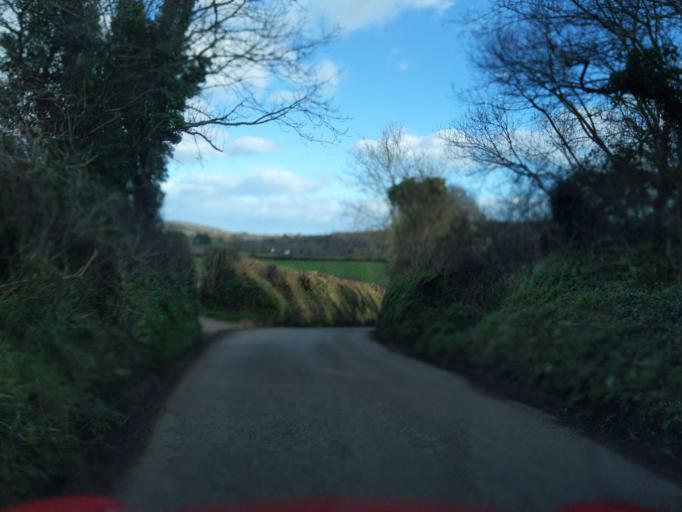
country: GB
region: England
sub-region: Devon
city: Salcombe
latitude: 50.2569
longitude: -3.7059
